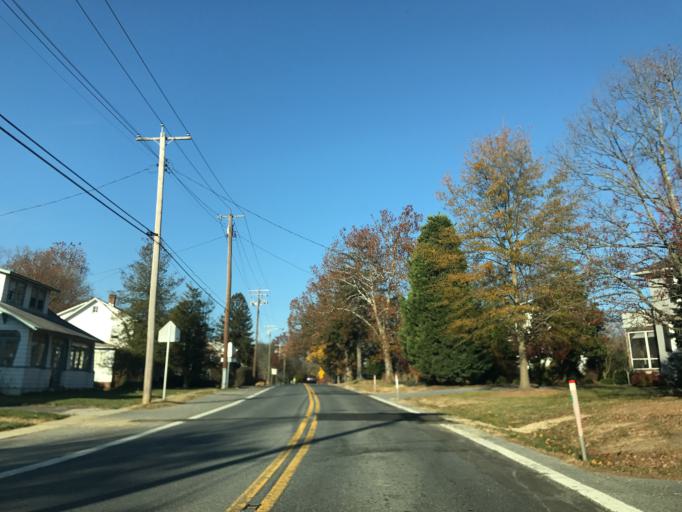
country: US
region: Maryland
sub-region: Baltimore County
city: Catonsville
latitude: 39.2661
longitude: -76.7425
